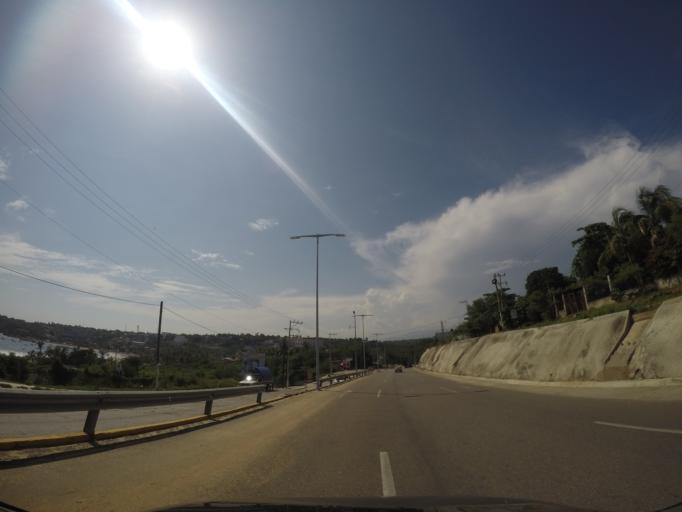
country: MX
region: Oaxaca
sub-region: San Pedro Mixtepec -Dto. 22 -
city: Puerto Escondido
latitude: 15.8592
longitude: -97.0580
